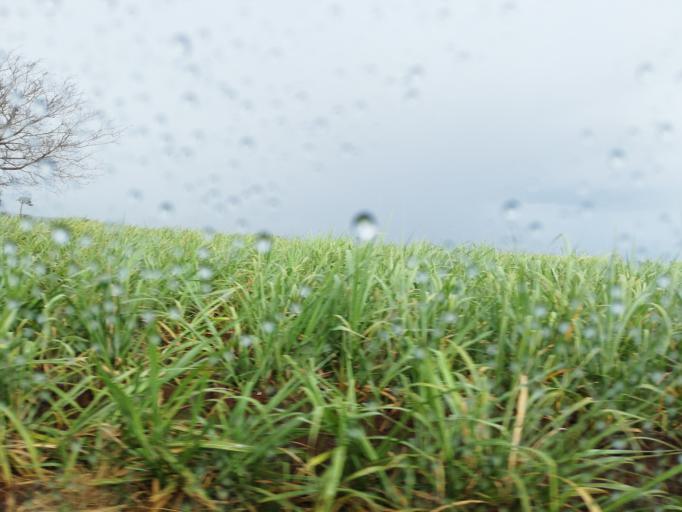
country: MU
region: Pamplemousses
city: Long Mountain
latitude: -20.1284
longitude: 57.5660
